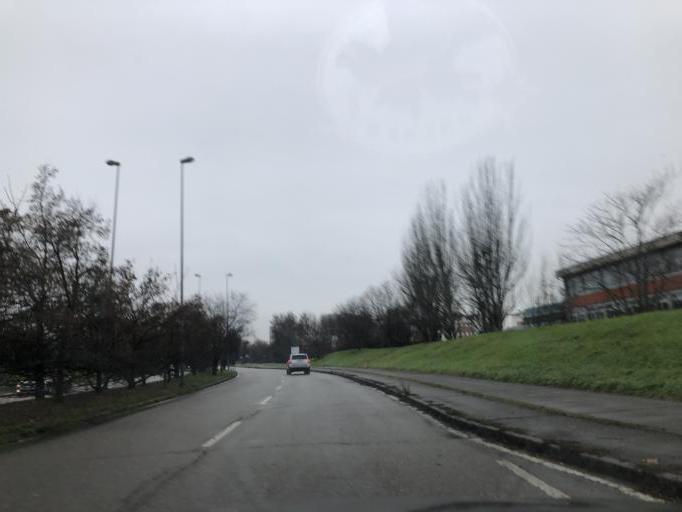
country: IT
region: Emilia-Romagna
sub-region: Provincia di Modena
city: Modena
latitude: 44.6409
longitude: 10.9015
